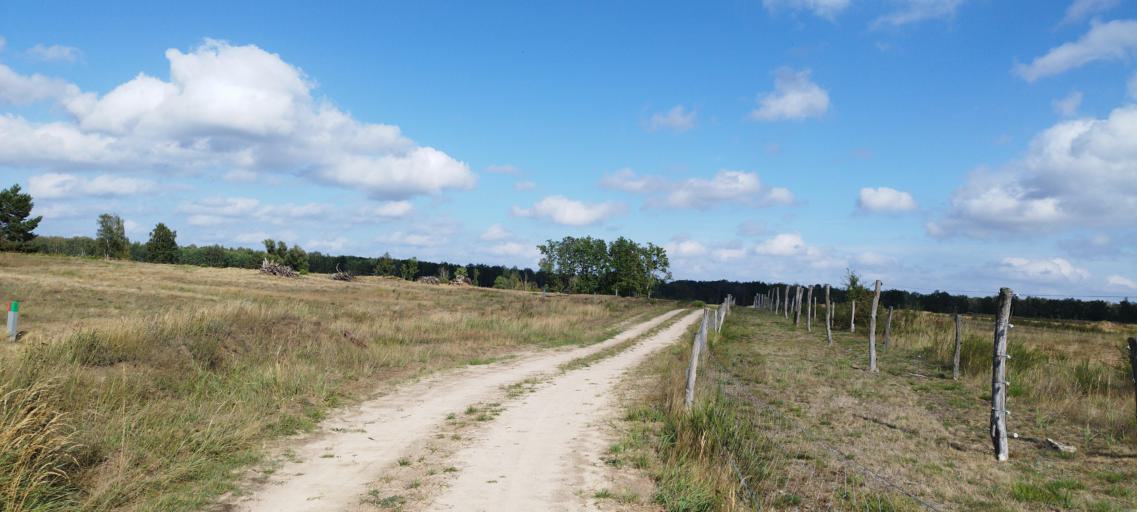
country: DE
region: Brandenburg
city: Dallgow-Doeberitz
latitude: 52.5253
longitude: 13.0265
